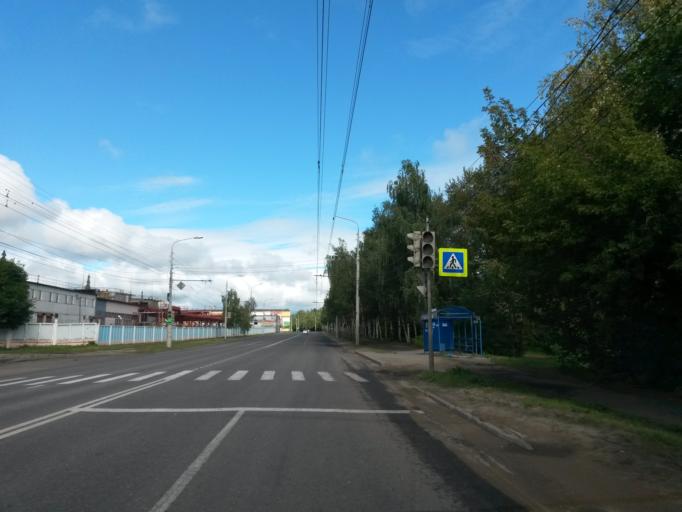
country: RU
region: Jaroslavl
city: Yaroslavl
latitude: 57.6484
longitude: 39.8789
